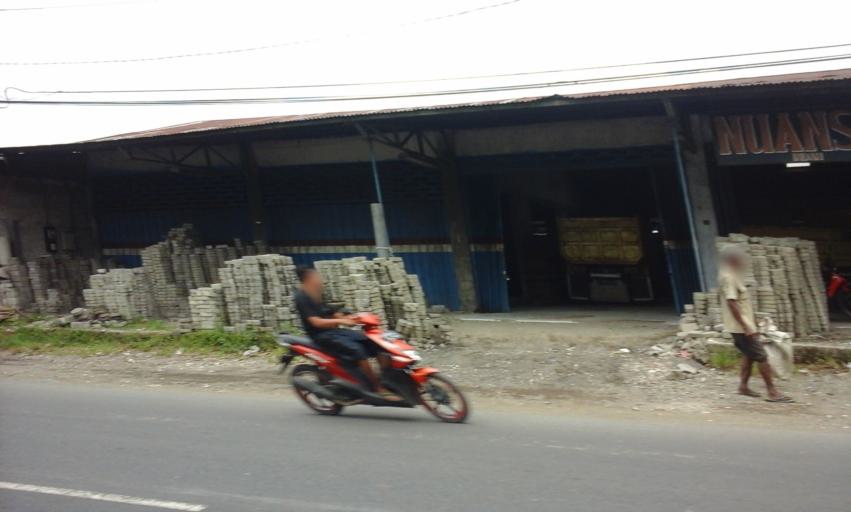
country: ID
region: East Java
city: Dukuhsia
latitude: -8.2024
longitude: 113.6178
